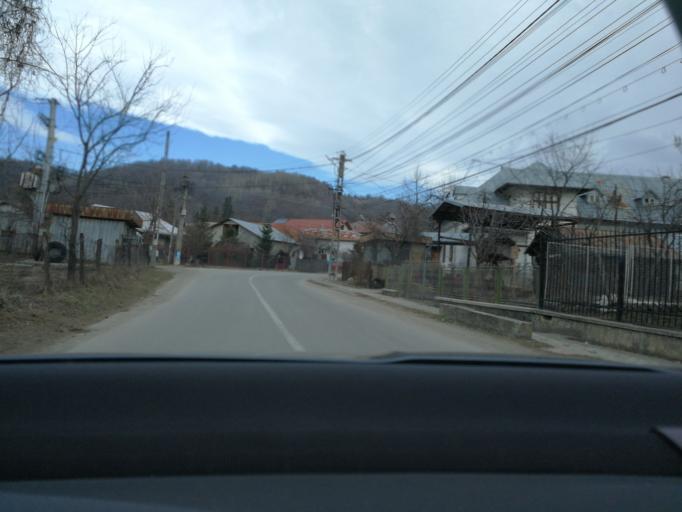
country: RO
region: Prahova
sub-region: Comuna Telega
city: Telega
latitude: 45.1374
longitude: 25.7873
